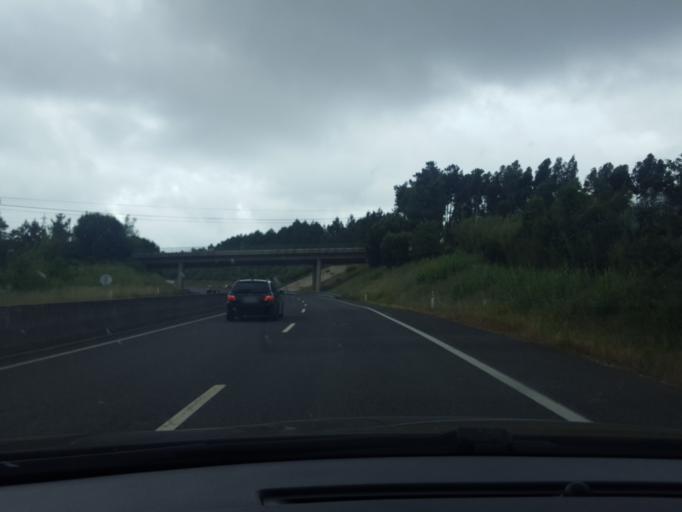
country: PT
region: Leiria
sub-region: Leiria
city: Leiria
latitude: 39.7576
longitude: -8.7753
